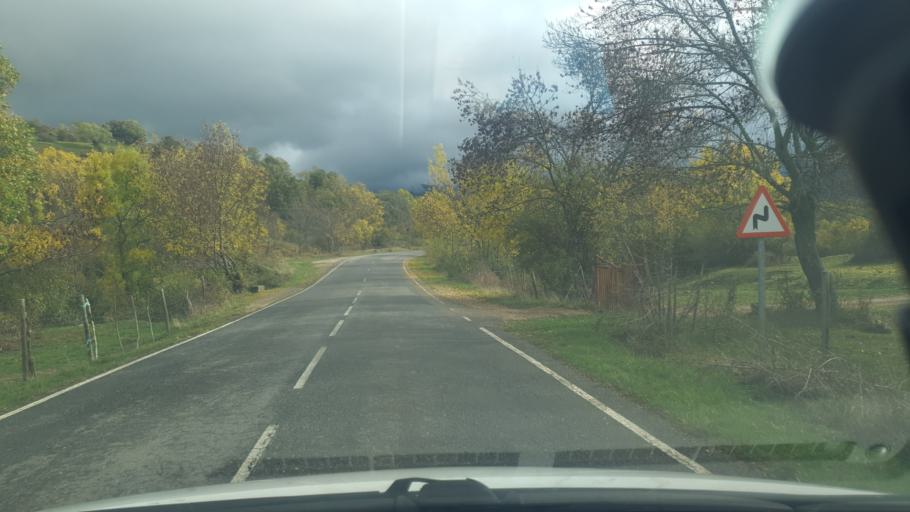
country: ES
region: Castille and Leon
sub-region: Provincia de Segovia
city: Gallegos
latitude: 41.0822
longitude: -3.7925
